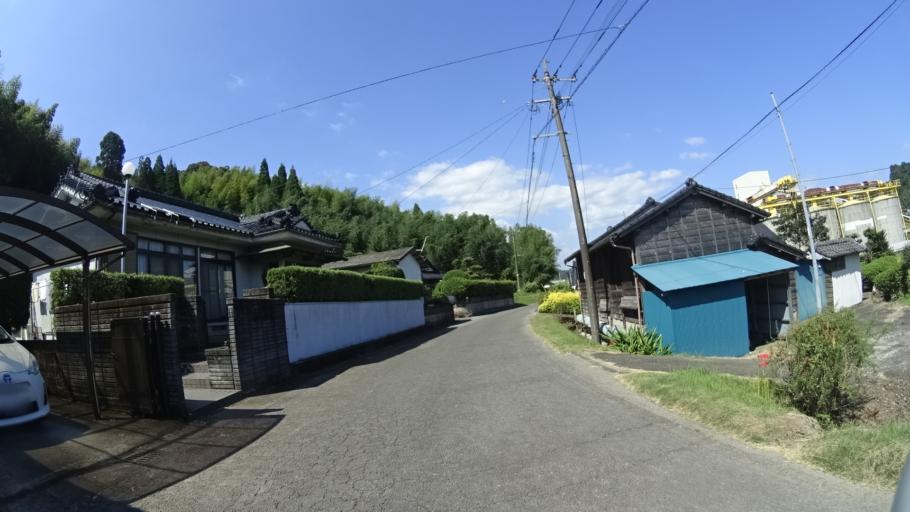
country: JP
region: Kagoshima
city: Kajiki
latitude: 31.7562
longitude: 130.6746
